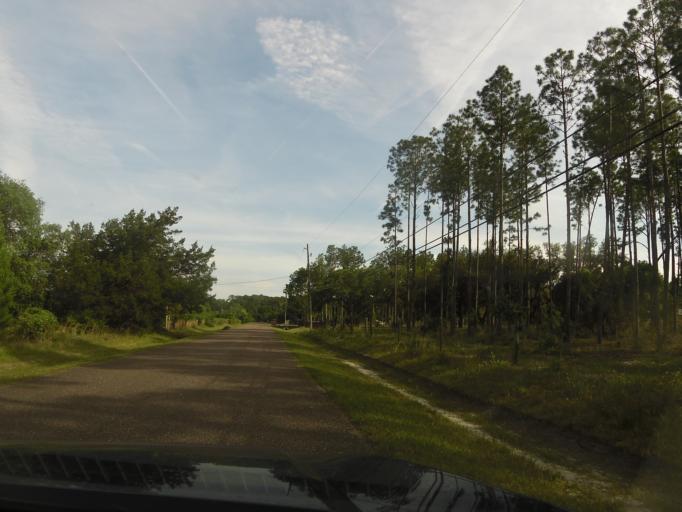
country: US
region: Florida
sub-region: Nassau County
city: Fernandina Beach
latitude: 30.5300
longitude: -81.4879
